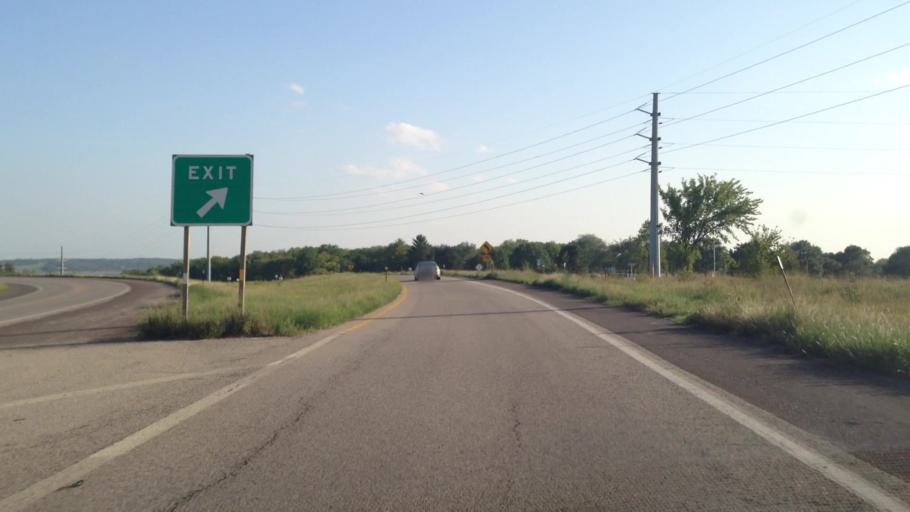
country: US
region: Kansas
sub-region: Douglas County
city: Lawrence
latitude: 38.9466
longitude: -95.3374
